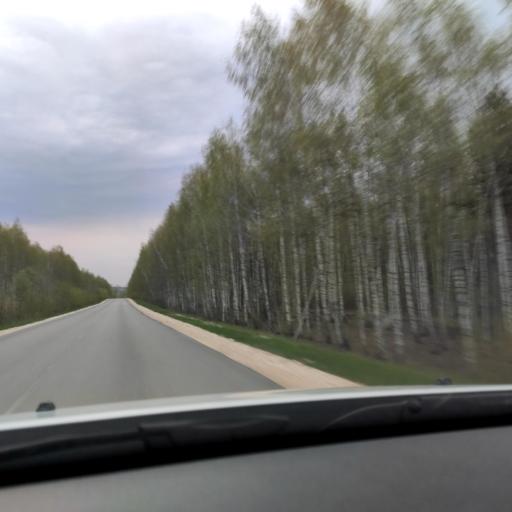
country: RU
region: Lipetsk
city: Donskoye
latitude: 52.6434
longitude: 38.9724
